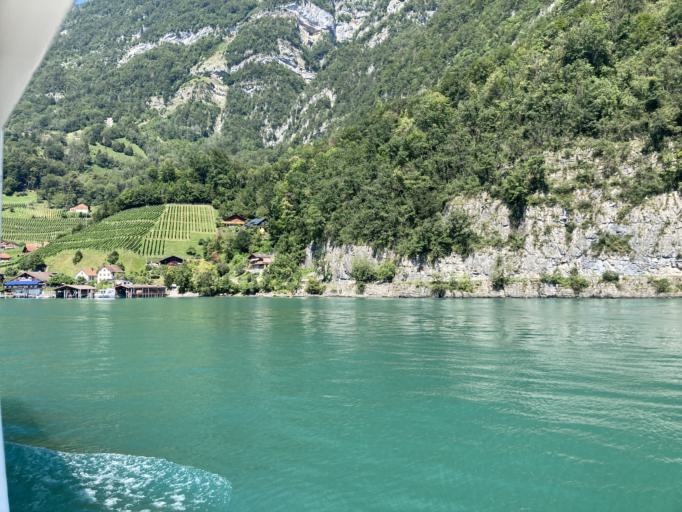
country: CH
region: Saint Gallen
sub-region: Wahlkreis Sarganserland
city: Quarten
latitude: 47.1275
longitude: 9.2201
